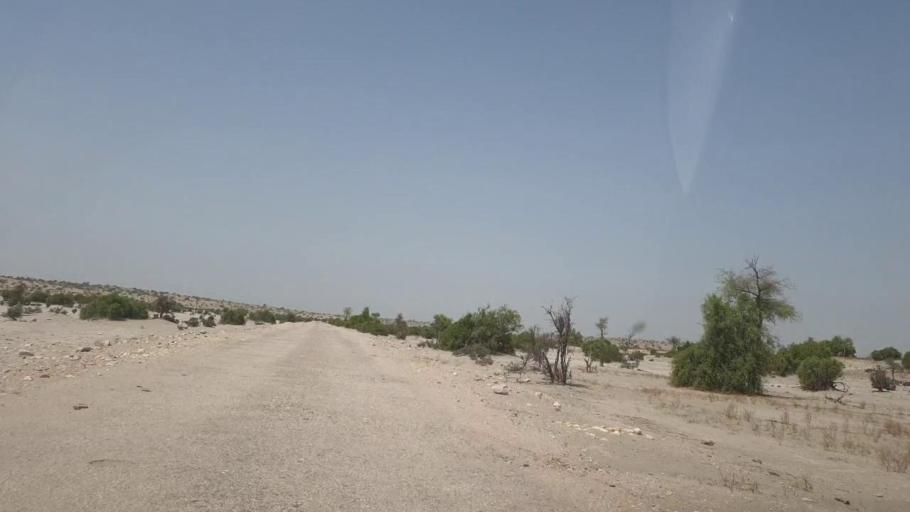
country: PK
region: Sindh
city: Khanpur
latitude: 27.3364
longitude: 69.3110
